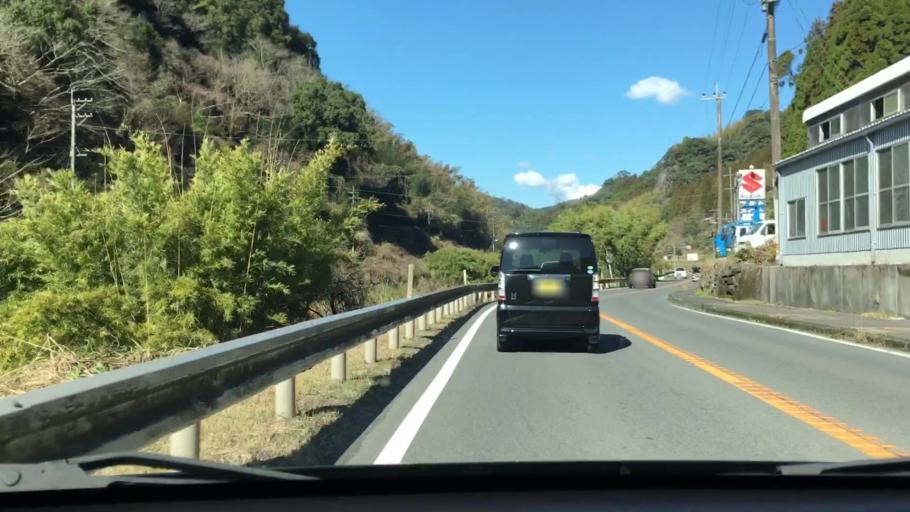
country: JP
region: Kagoshima
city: Kagoshima-shi
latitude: 31.6454
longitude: 130.5143
